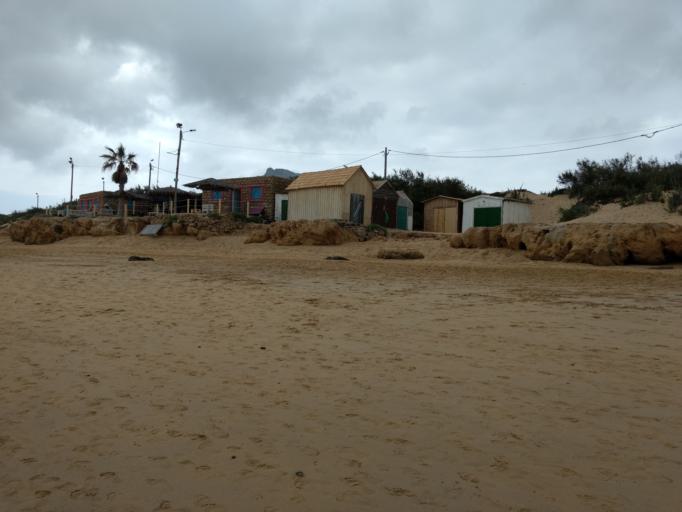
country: PT
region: Madeira
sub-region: Porto Santo
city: Vila de Porto Santo
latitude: 33.0443
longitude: -16.3511
